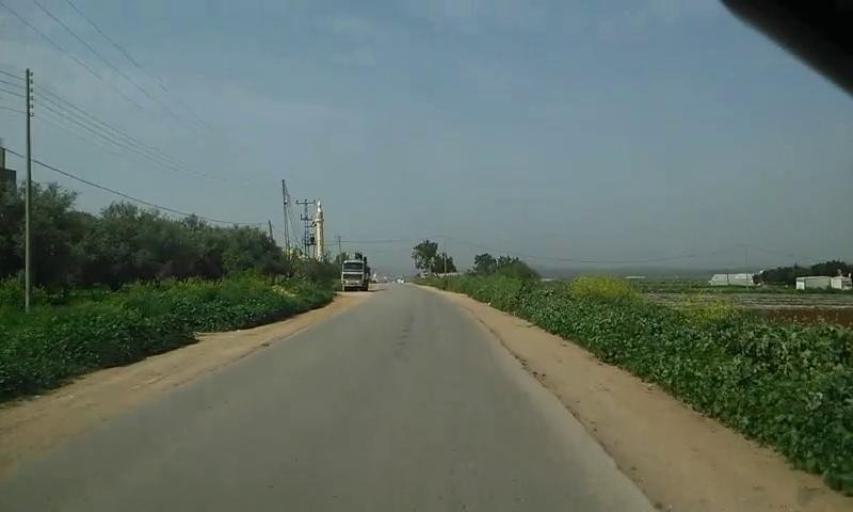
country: PS
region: West Bank
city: Kafr Dan
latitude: 32.4956
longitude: 35.2544
